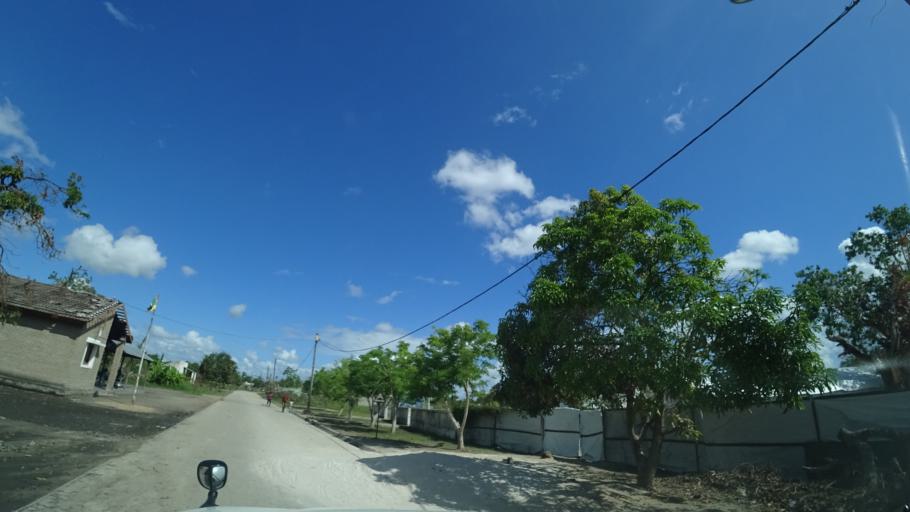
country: MZ
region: Sofala
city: Dondo
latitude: -19.4957
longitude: 34.5984
